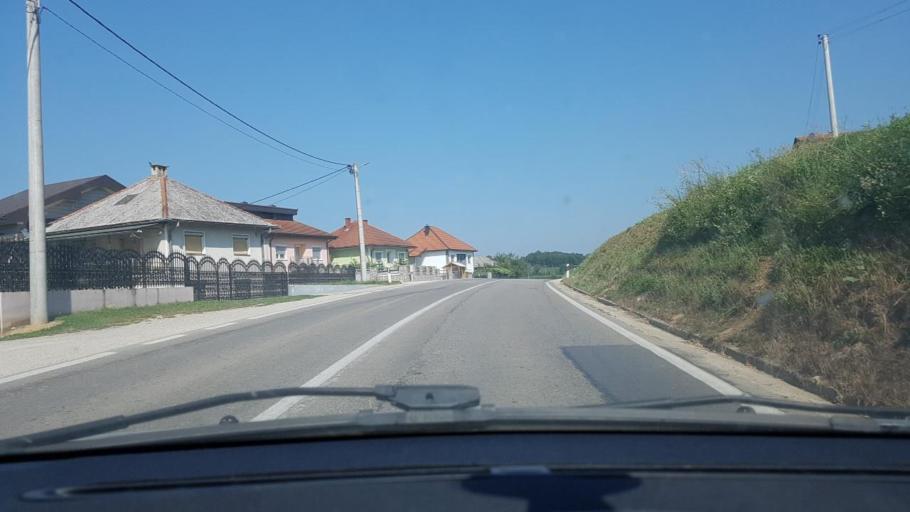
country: BA
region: Federation of Bosnia and Herzegovina
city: Mala Kladusa
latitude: 45.1344
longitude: 15.8507
